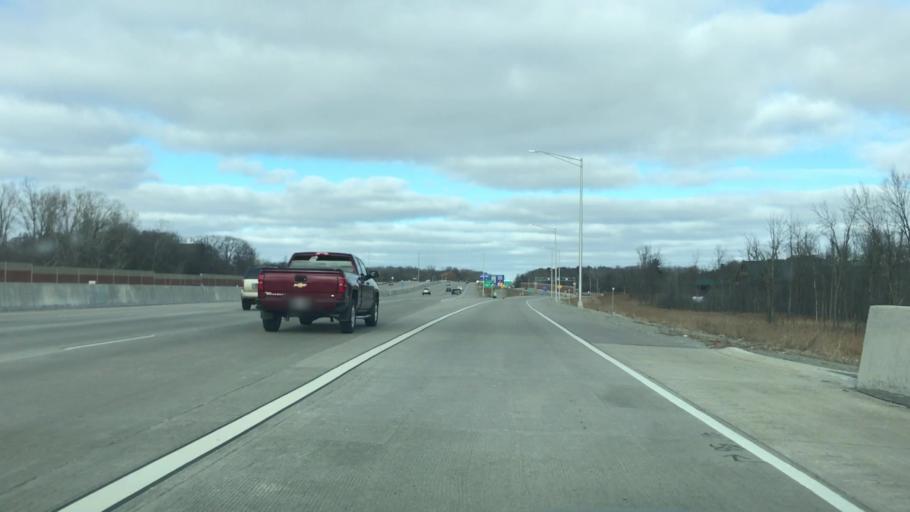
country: US
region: Wisconsin
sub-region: Brown County
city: Ashwaubenon
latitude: 44.5042
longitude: -88.0820
